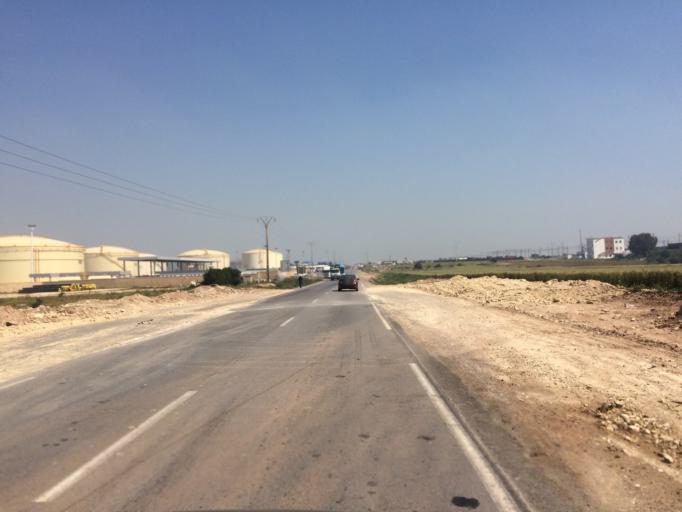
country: MA
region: Doukkala-Abda
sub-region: El-Jadida
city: Moulay Abdallah
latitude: 33.1433
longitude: -8.6079
